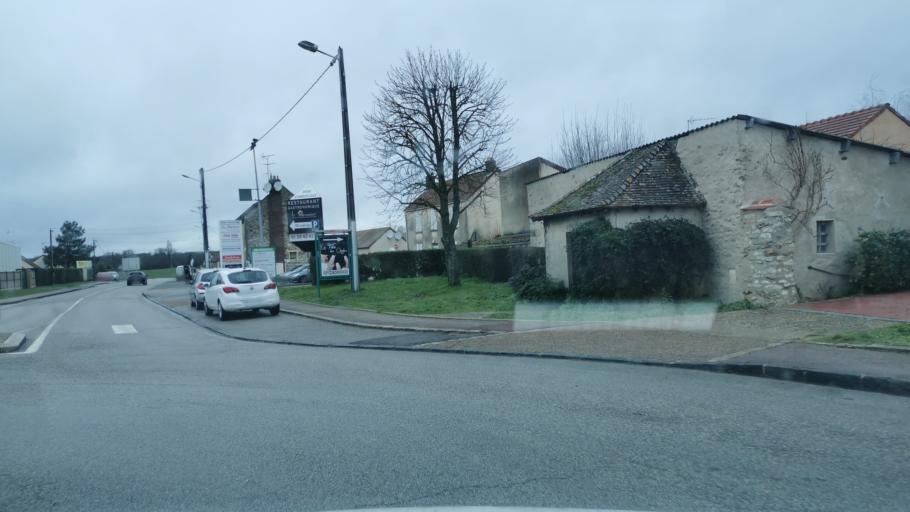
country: FR
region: Ile-de-France
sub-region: Departement des Yvelines
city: Longnes
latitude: 48.9208
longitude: 1.5844
